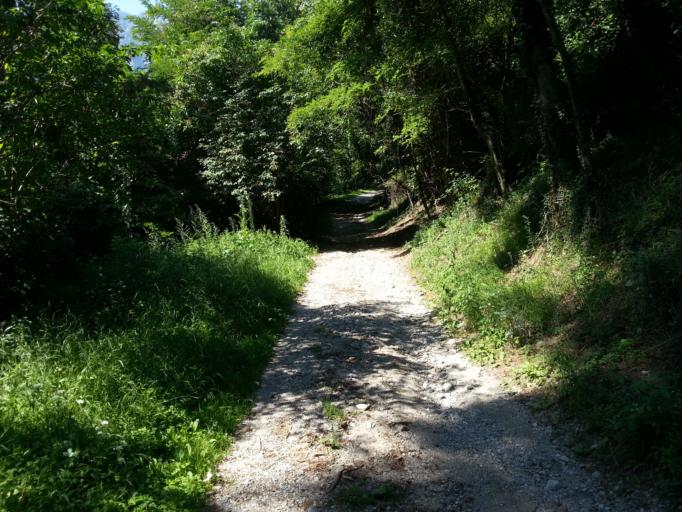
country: IT
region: Lombardy
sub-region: Provincia di Lecco
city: Ballabio
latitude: 45.8740
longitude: 9.4124
